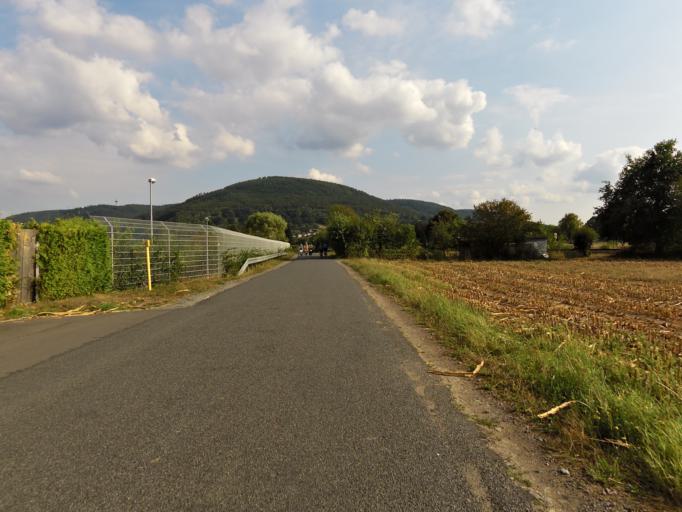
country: DE
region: Bavaria
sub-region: Regierungsbezirk Unterfranken
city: Kleinheubach
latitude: 49.7116
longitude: 9.2252
